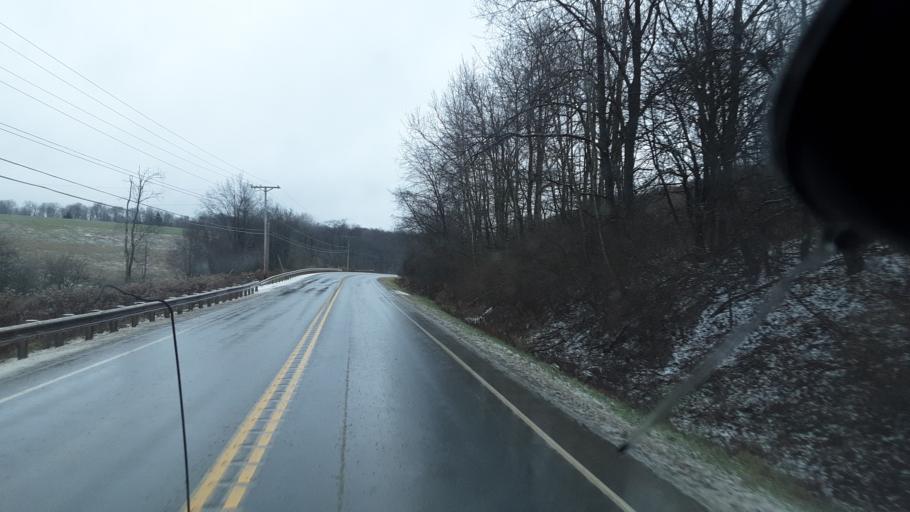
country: US
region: Pennsylvania
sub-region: Potter County
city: Coudersport
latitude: 41.8426
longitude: -77.8890
